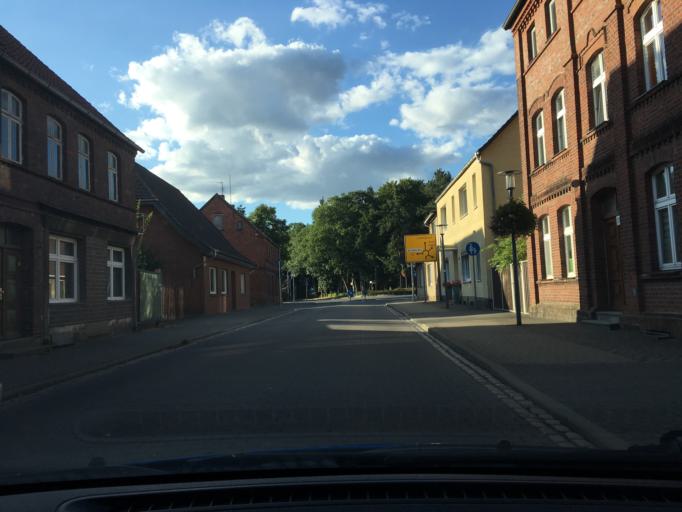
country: DE
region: Mecklenburg-Vorpommern
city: Grabow
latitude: 53.2821
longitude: 11.5589
